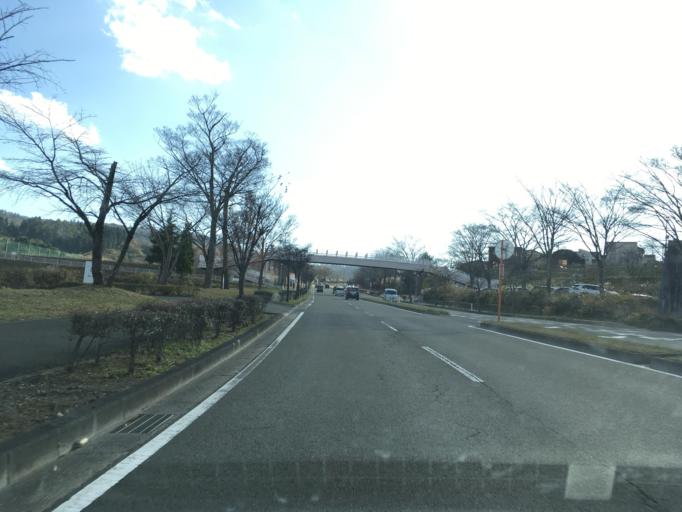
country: JP
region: Miyagi
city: Sendai
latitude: 38.2649
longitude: 140.7614
